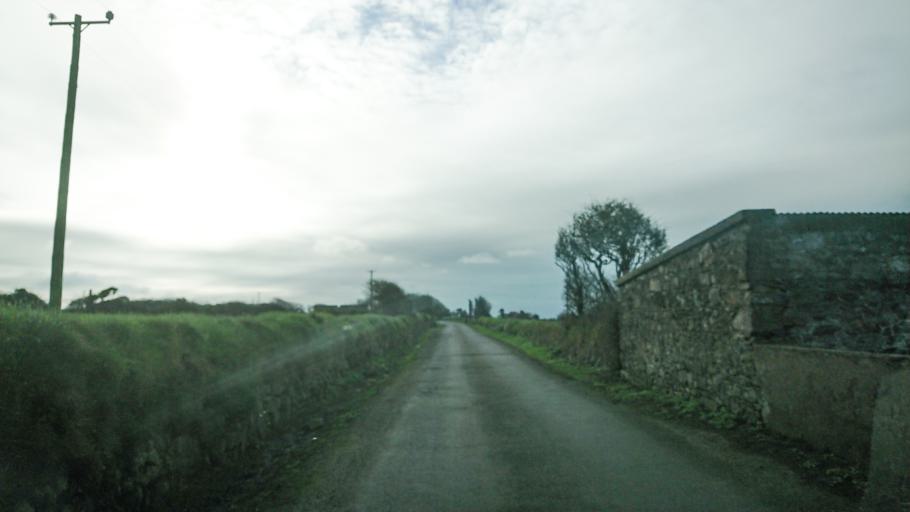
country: IE
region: Munster
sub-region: Waterford
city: Tra Mhor
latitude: 52.1419
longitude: -7.1945
